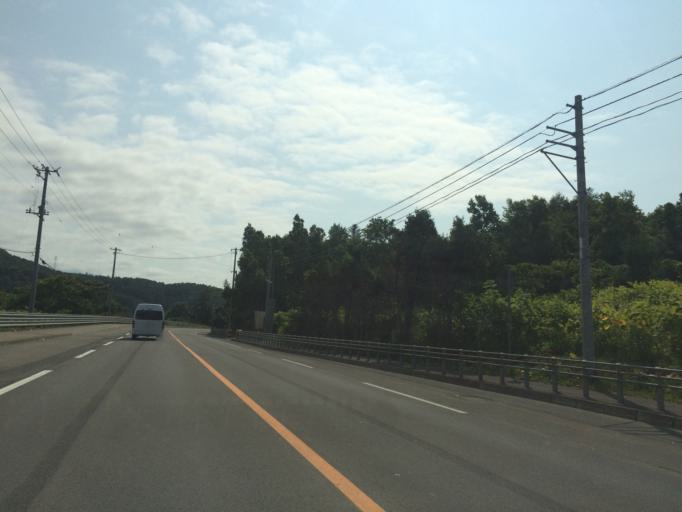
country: JP
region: Hokkaido
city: Yoichi
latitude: 43.2001
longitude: 140.8669
